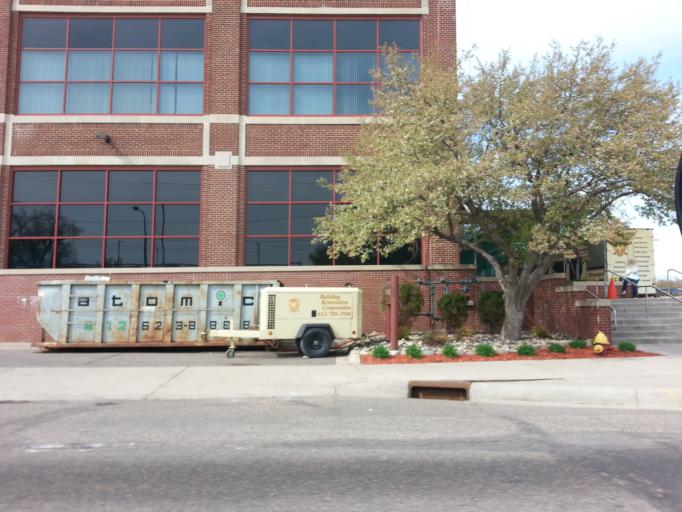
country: US
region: Minnesota
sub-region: Ramsey County
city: Lauderdale
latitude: 44.9647
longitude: -93.2037
